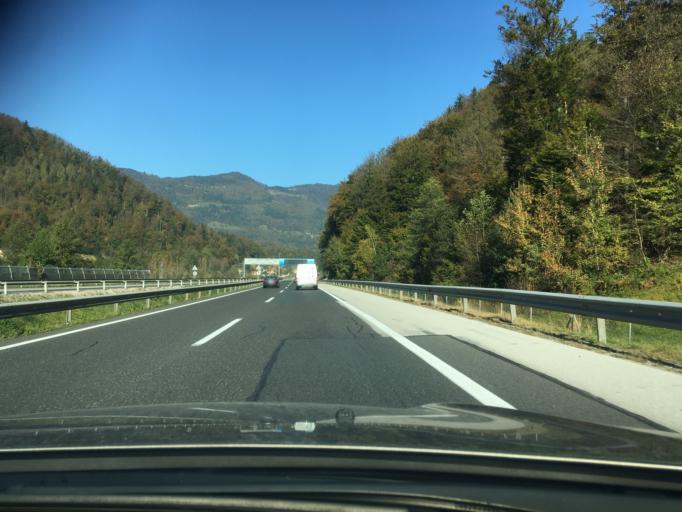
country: SI
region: Vransko
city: Vransko
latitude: 46.2286
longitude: 14.9491
